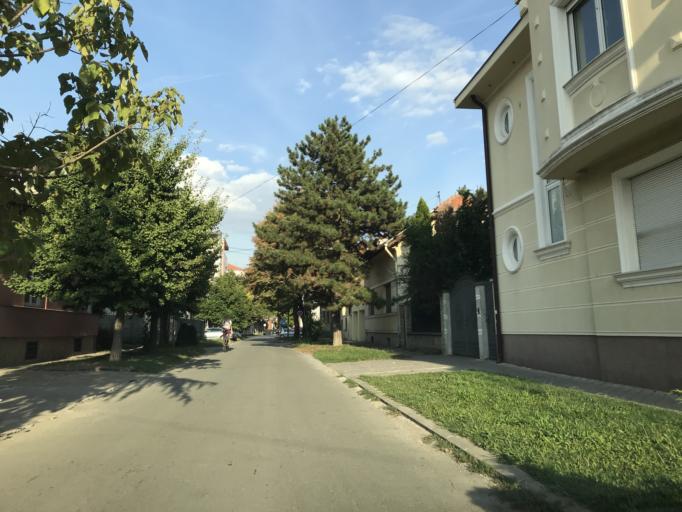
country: RS
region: Autonomna Pokrajina Vojvodina
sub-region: Juznobacki Okrug
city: Novi Sad
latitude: 45.2530
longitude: 19.8294
